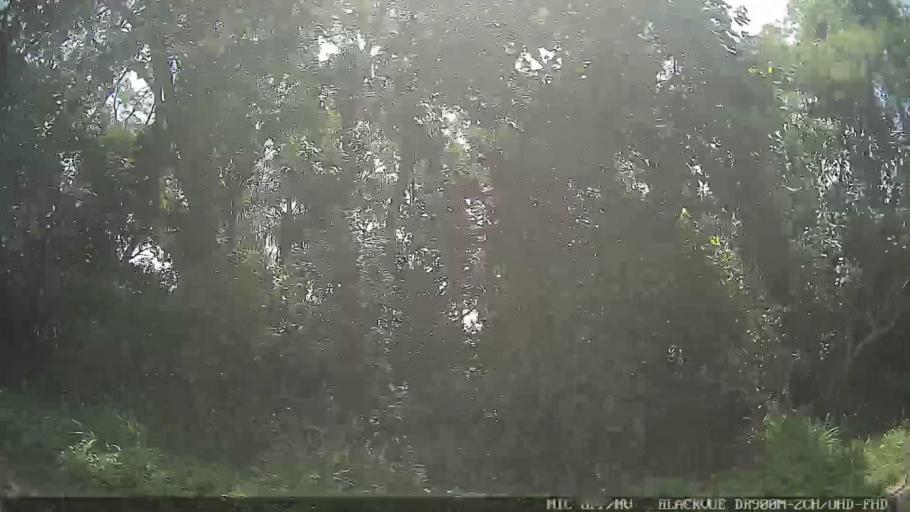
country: BR
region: Sao Paulo
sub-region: Ferraz De Vasconcelos
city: Ferraz de Vasconcelos
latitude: -23.6109
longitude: -46.3715
